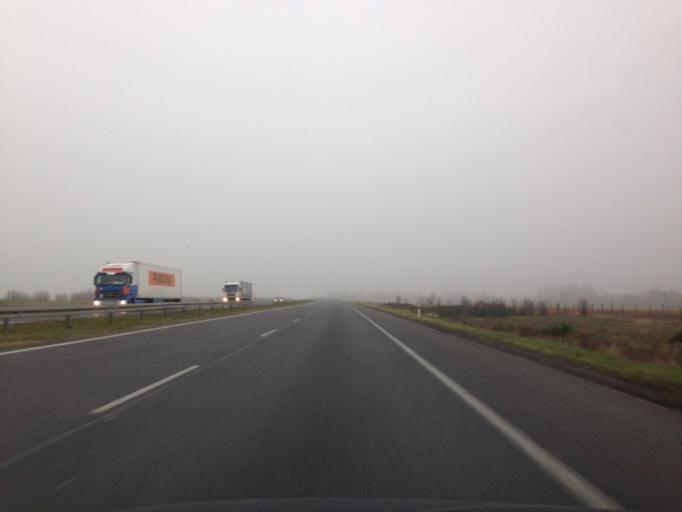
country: PL
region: Lodz Voivodeship
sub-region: Powiat radomszczanski
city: Kamiensk
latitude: 51.2753
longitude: 19.5328
